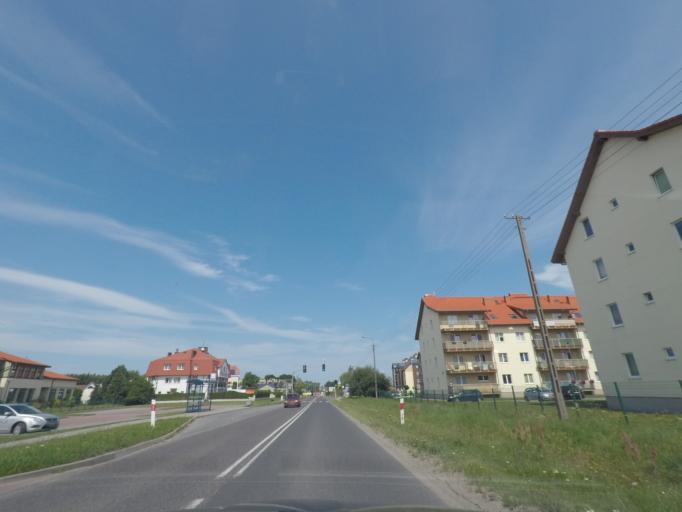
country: PL
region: Pomeranian Voivodeship
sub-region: Powiat slupski
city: Ustka
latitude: 54.5730
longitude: 16.8519
